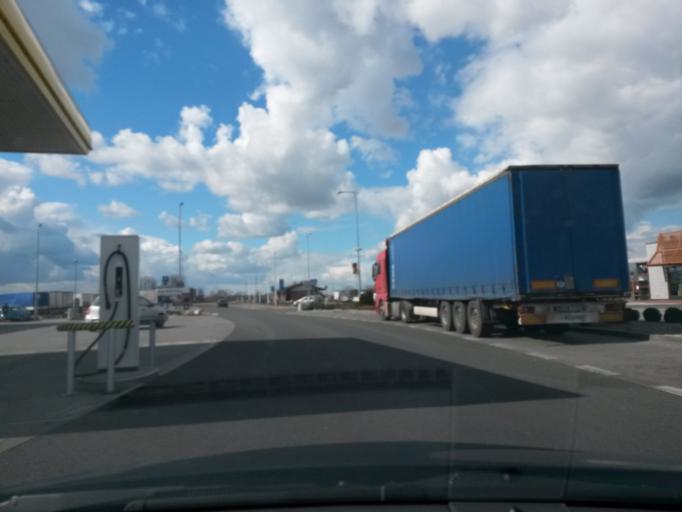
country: PL
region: Greater Poland Voivodeship
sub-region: Powiat turecki
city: Brudzew
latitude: 52.1356
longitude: 18.6350
